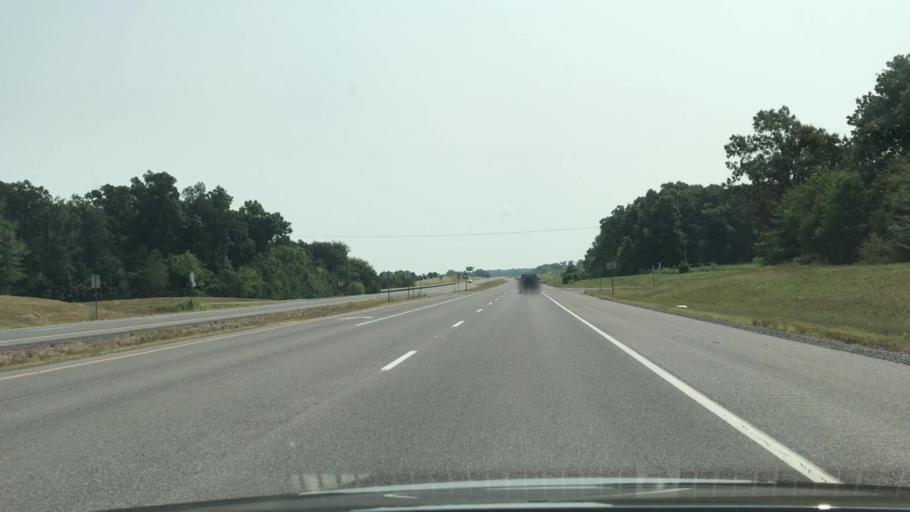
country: US
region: Kentucky
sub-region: Calloway County
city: Murray
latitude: 36.6503
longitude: -88.2641
